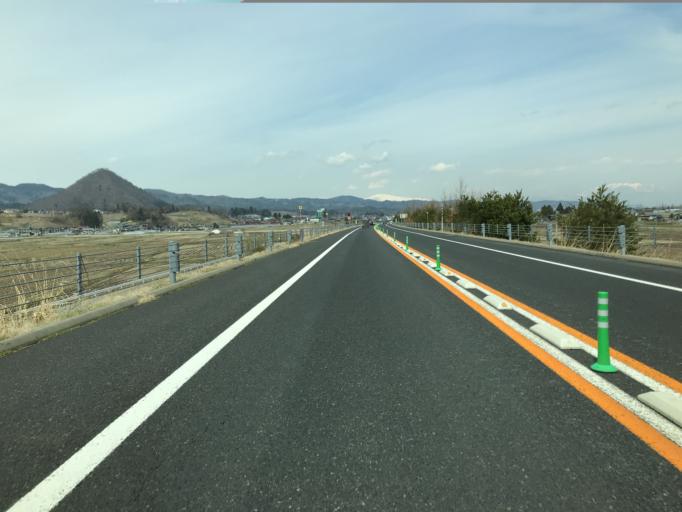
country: JP
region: Yamagata
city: Kaminoyama
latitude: 38.2213
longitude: 140.2820
